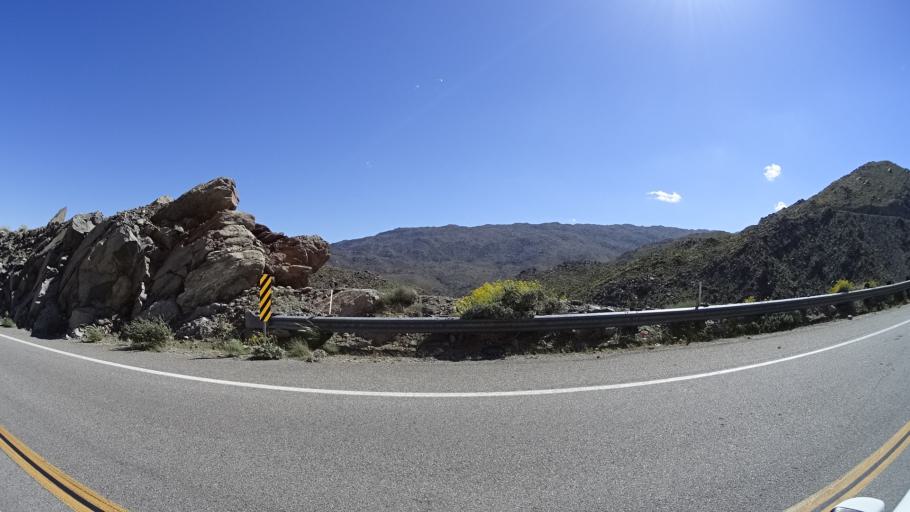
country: US
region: California
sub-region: San Diego County
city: Borrego Springs
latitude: 33.2244
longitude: -116.4162
